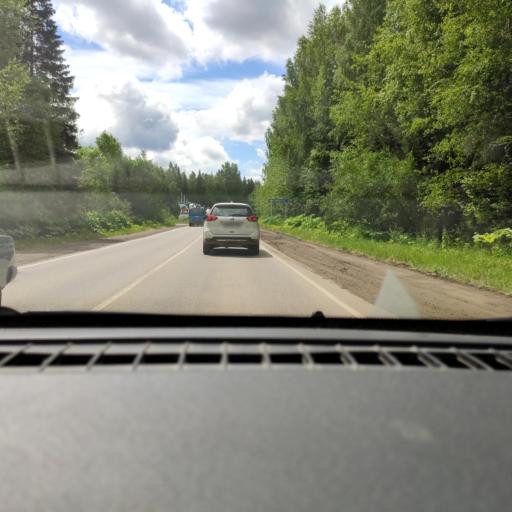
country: RU
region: Perm
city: Overyata
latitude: 58.1109
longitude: 55.8290
